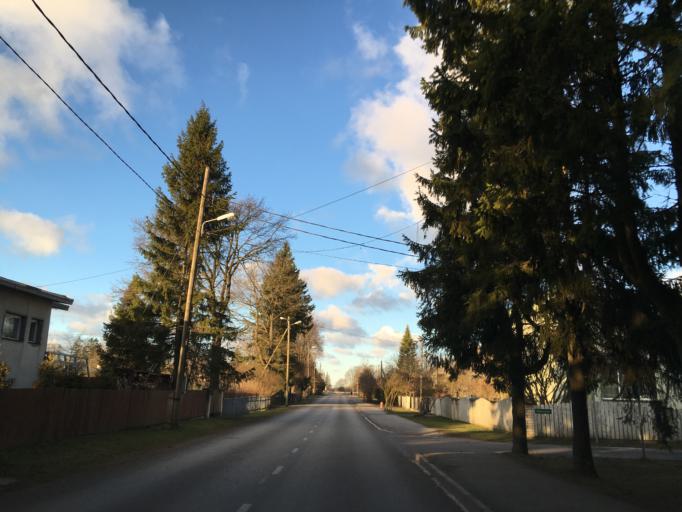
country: EE
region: Harju
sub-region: Saue linn
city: Saue
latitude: 59.3226
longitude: 24.5506
